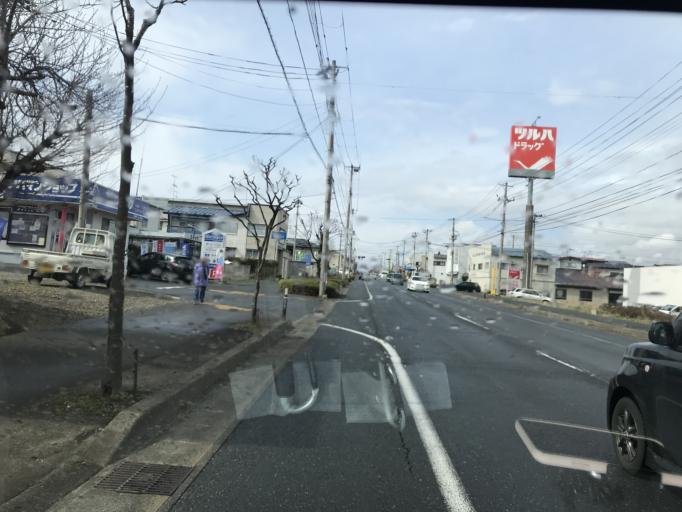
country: JP
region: Iwate
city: Kitakami
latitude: 39.3049
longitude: 141.1158
